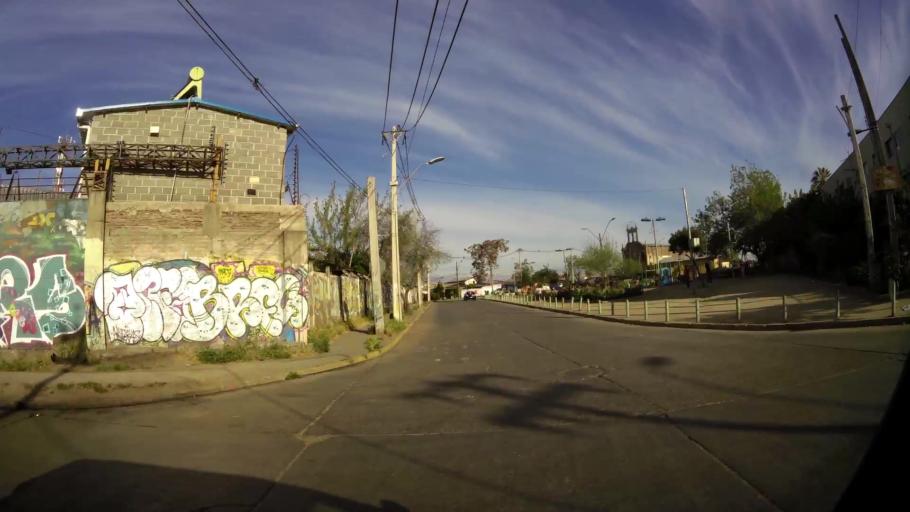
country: CL
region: Santiago Metropolitan
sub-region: Provincia de Santiago
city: Lo Prado
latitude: -33.4691
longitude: -70.7022
